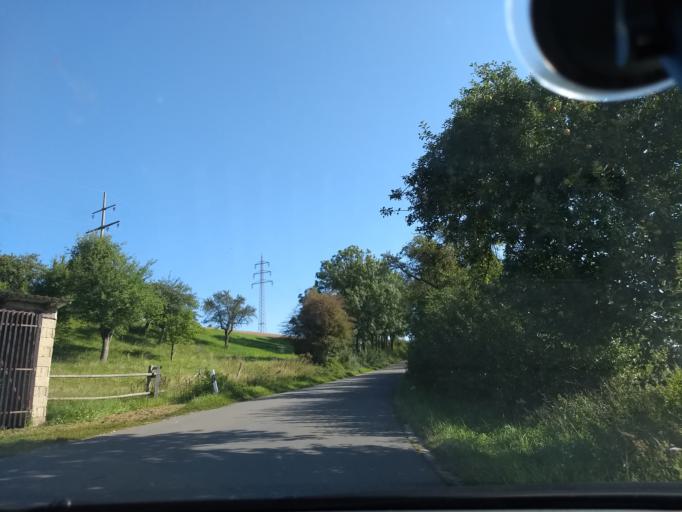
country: DE
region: North Rhine-Westphalia
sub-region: Regierungsbezirk Detmold
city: Buren
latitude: 51.5468
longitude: 8.5256
